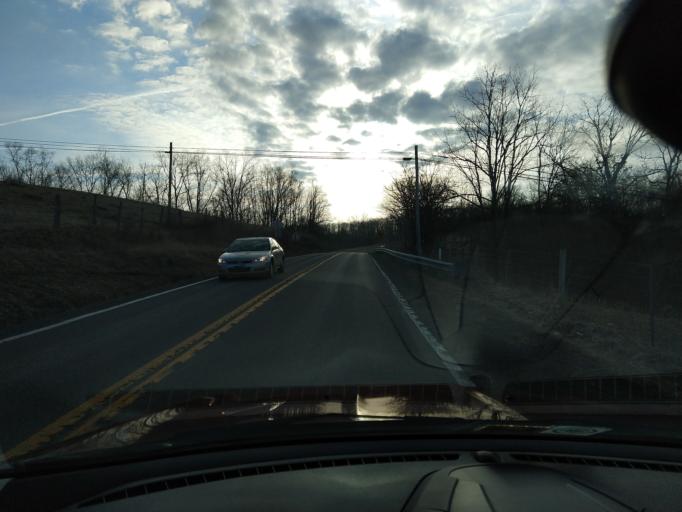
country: US
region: West Virginia
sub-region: Pocahontas County
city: Marlinton
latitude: 38.1222
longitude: -80.2396
